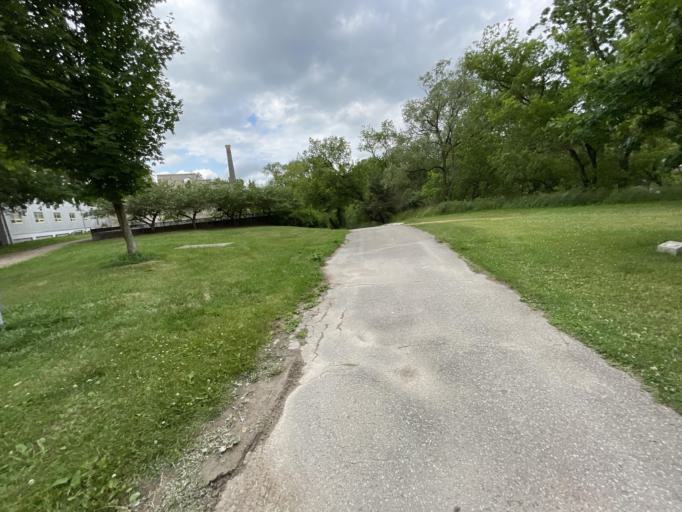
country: CA
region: Ontario
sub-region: Wellington County
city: Guelph
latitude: 43.5504
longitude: -80.2535
